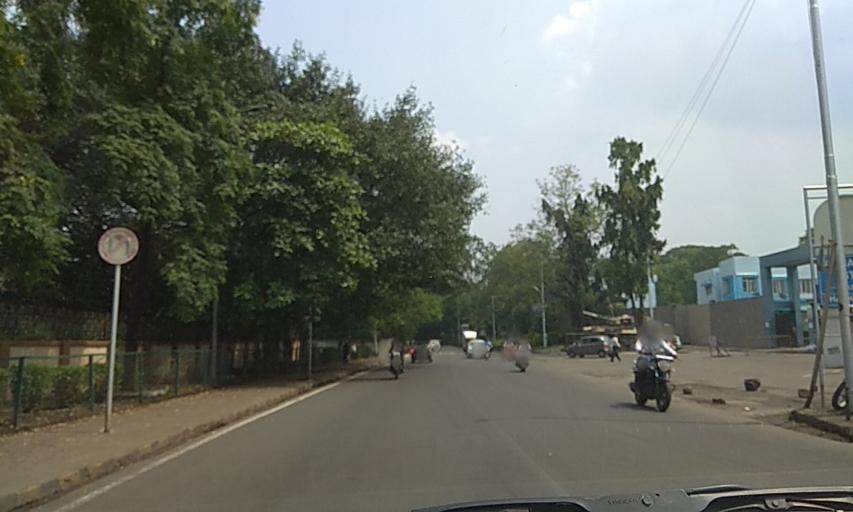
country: IN
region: Maharashtra
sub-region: Pune Division
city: Shivaji Nagar
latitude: 18.5379
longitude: 73.8024
